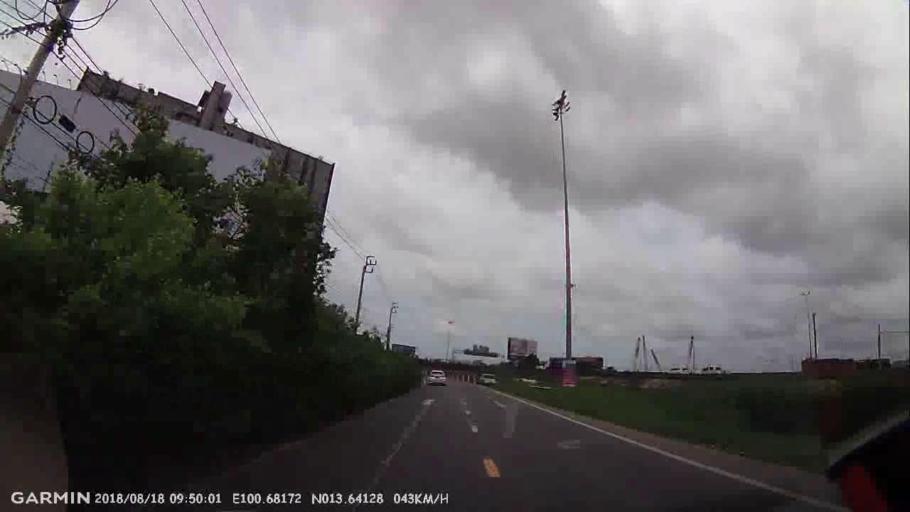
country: TH
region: Bangkok
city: Bang Na
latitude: 13.6412
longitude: 100.6816
